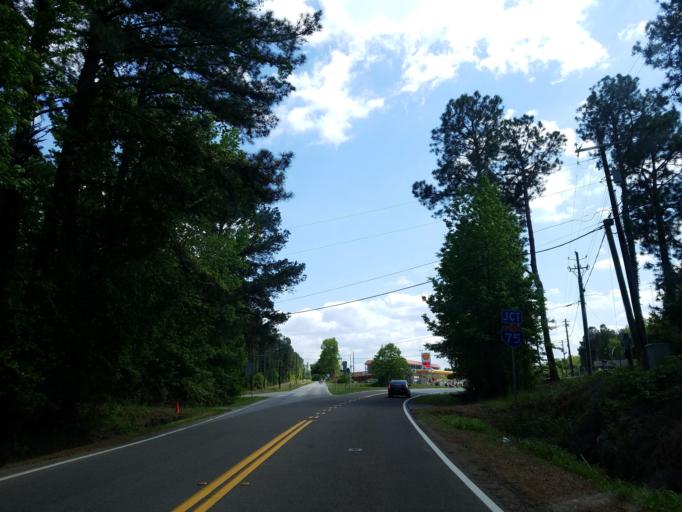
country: US
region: Georgia
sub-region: Monroe County
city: Forsyth
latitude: 33.0570
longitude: -83.9506
